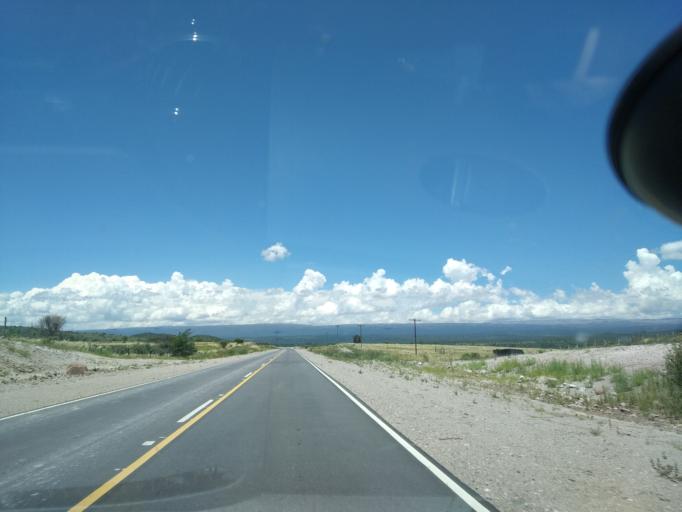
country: AR
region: Cordoba
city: Salsacate
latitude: -31.3528
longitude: -65.1282
